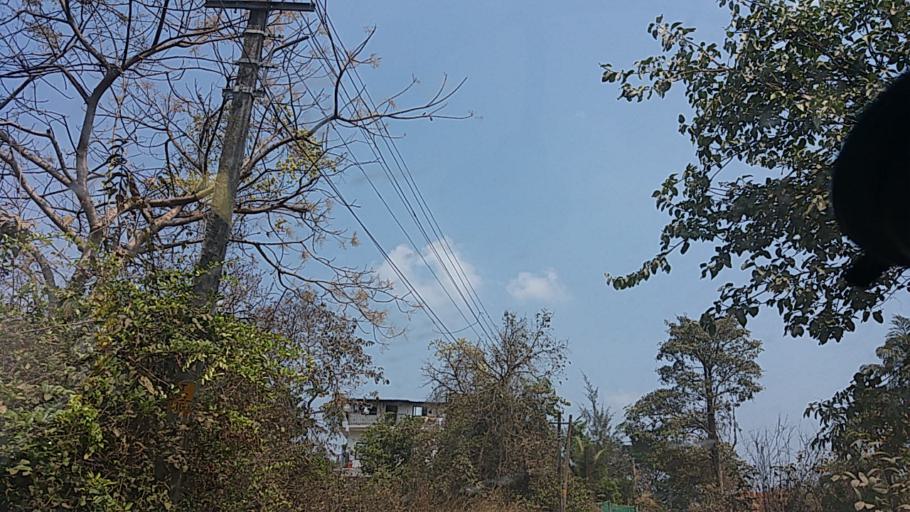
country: IN
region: Goa
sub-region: South Goa
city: Sancoale
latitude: 15.3762
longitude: 73.9126
